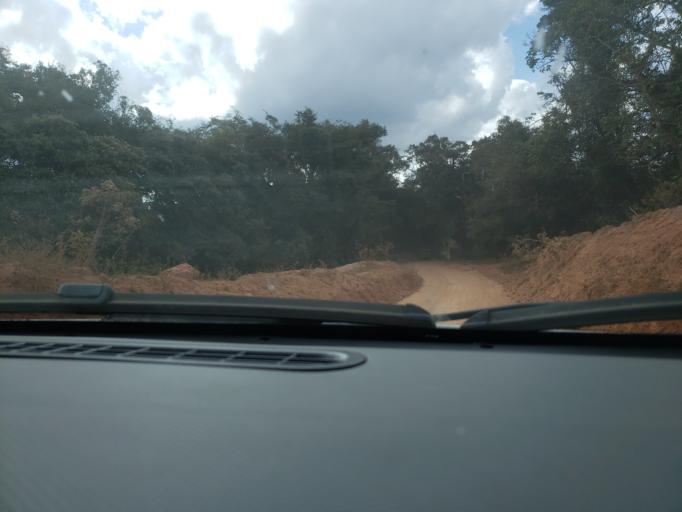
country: BR
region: Minas Gerais
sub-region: Campo Belo
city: Campo Belo
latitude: -20.9184
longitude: -45.2946
